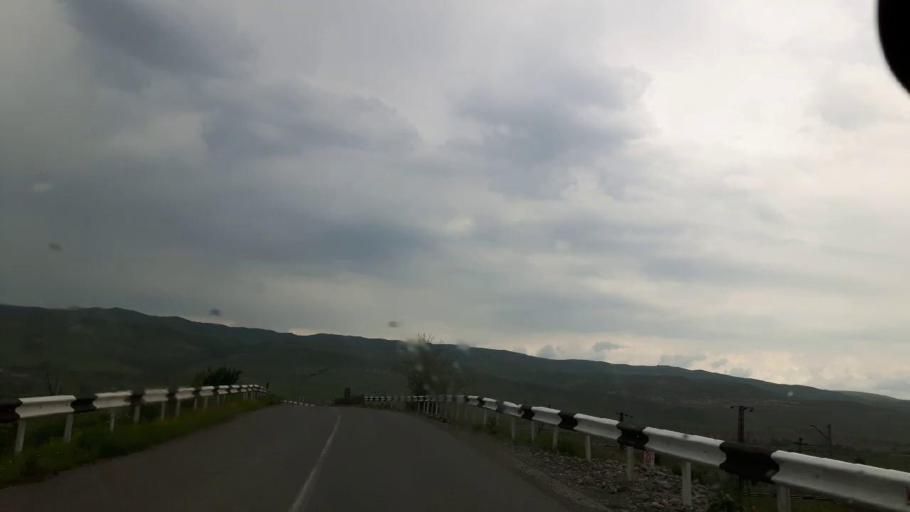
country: GE
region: Shida Kartli
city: Gori
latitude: 41.9637
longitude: 44.1866
